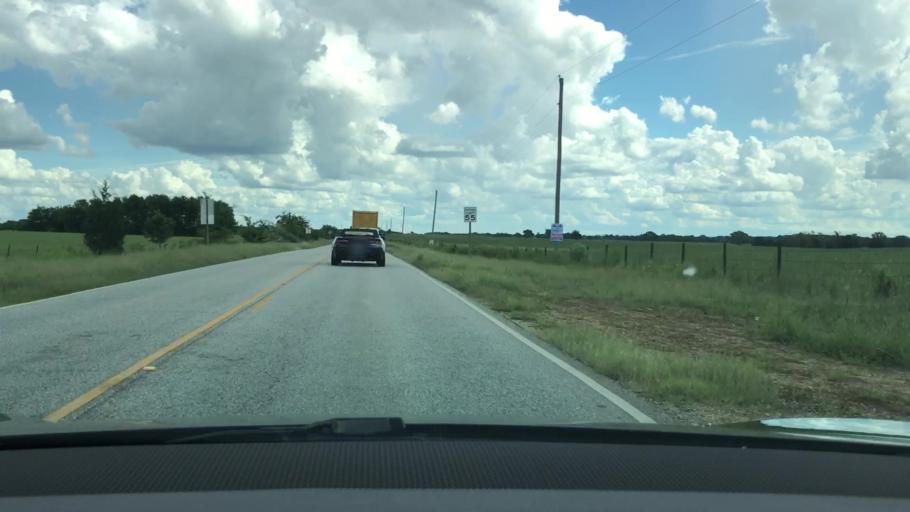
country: US
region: Alabama
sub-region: Montgomery County
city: Pike Road
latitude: 32.2786
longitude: -86.1019
